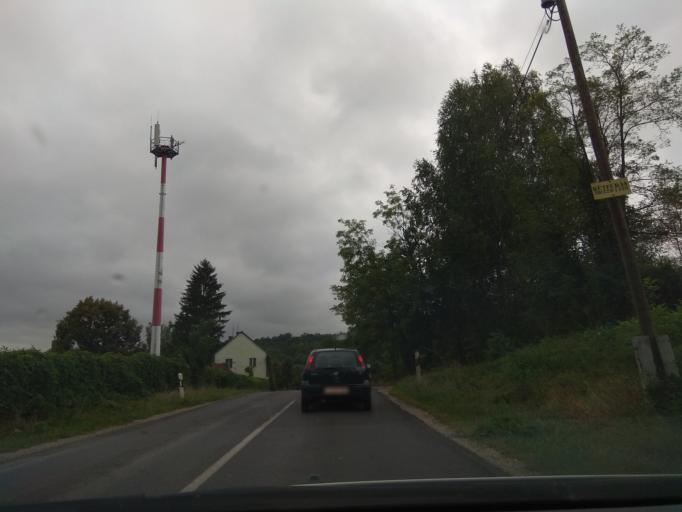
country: HU
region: Borsod-Abauj-Zemplen
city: Harsany
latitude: 47.9999
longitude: 20.7587
